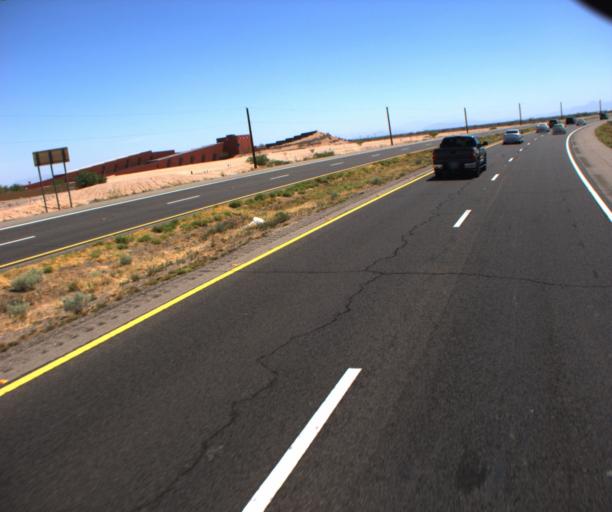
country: US
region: Arizona
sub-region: Maricopa County
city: Sun Lakes
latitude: 33.2510
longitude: -111.9754
